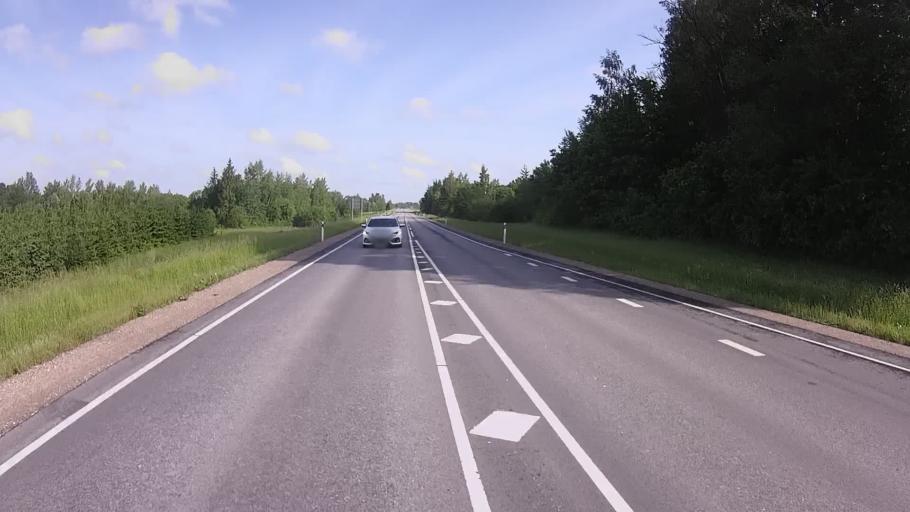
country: EE
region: Viljandimaa
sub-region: Viljandi linn
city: Viljandi
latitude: 58.3472
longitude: 25.5640
